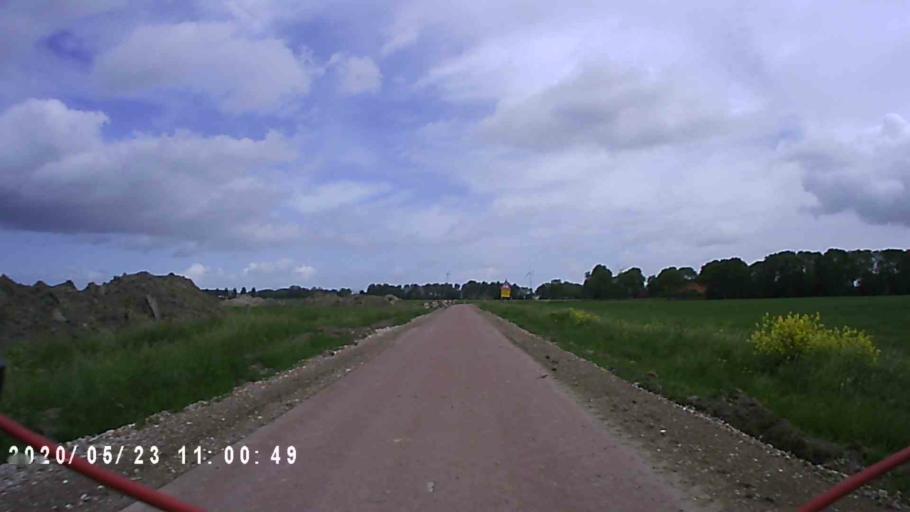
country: NL
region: Groningen
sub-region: Gemeente Delfzijl
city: Delfzijl
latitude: 53.3070
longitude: 6.9433
